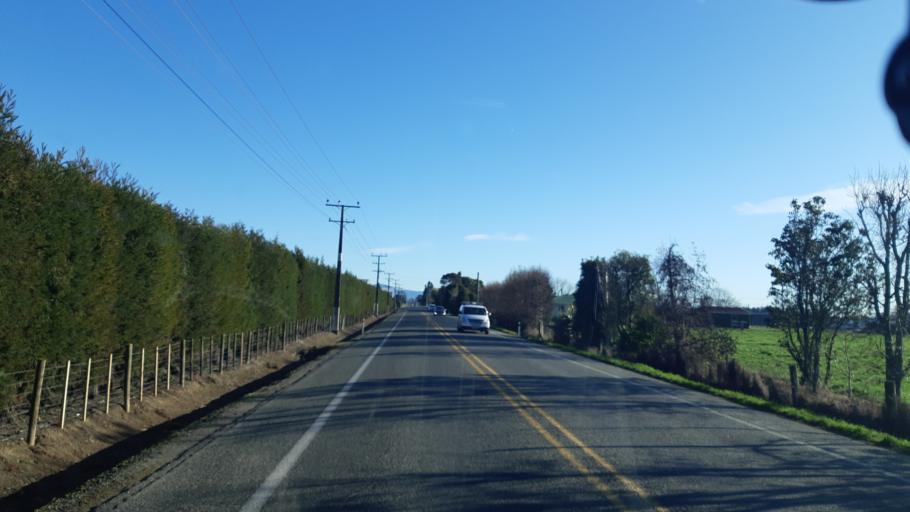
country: NZ
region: Tasman
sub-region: Tasman District
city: Richmond
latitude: -41.3218
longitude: 173.1417
